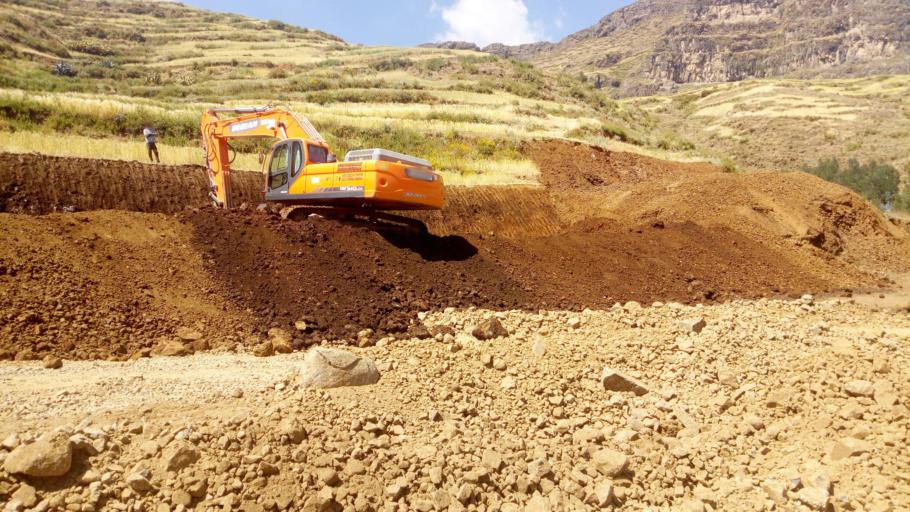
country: ET
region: Tigray
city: Maych'ew
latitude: 12.9853
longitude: 39.4485
